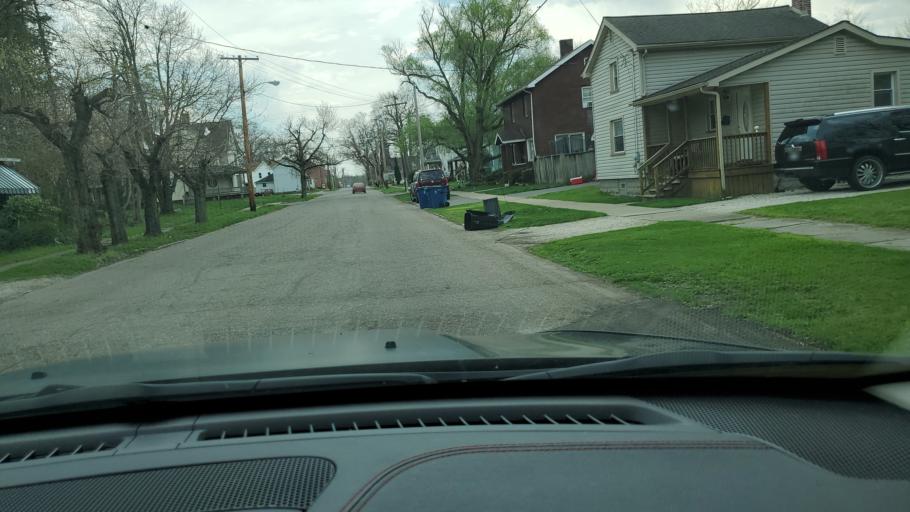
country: US
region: Ohio
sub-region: Trumbull County
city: Niles
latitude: 41.1840
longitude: -80.7667
